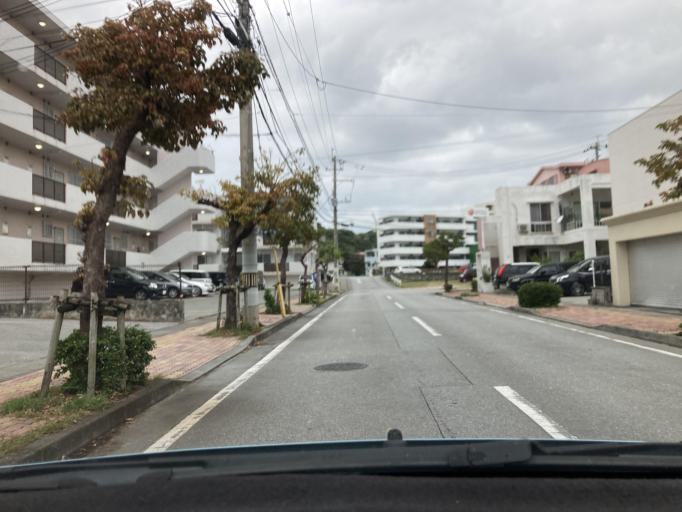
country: JP
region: Okinawa
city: Okinawa
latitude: 26.3159
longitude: 127.8228
